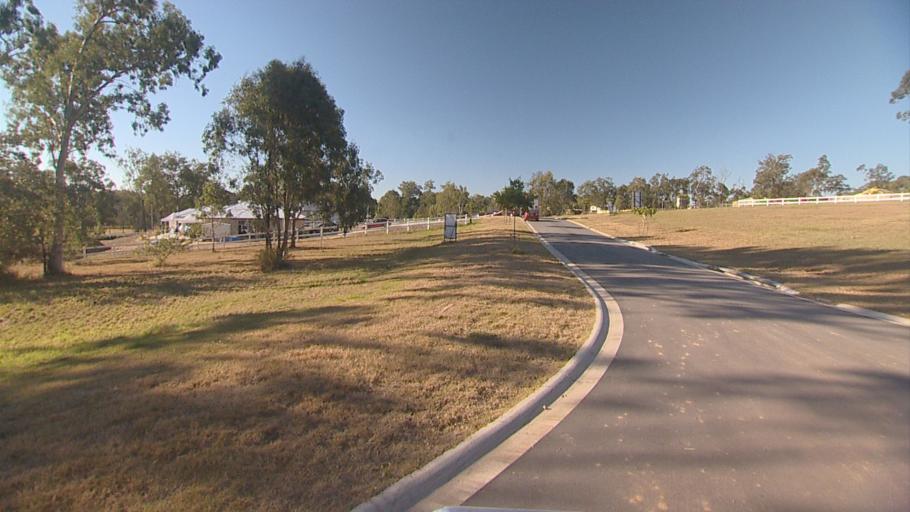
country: AU
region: Queensland
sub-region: Logan
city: North Maclean
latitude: -27.7940
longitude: 153.0222
